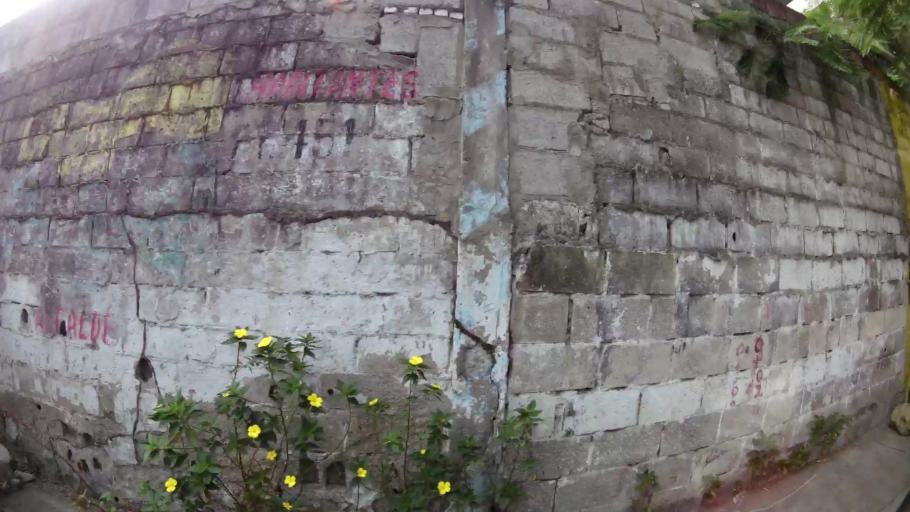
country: EC
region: Guayas
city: Guayaquil
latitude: -2.2523
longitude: -79.8766
